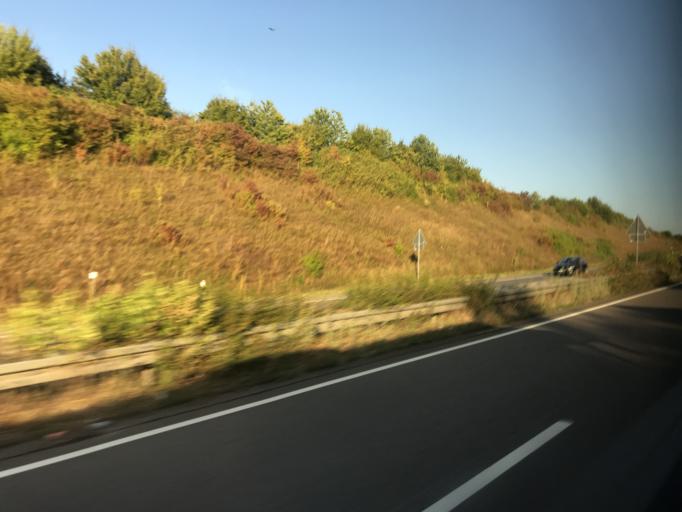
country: DE
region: Saarland
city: Perl
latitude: 49.4802
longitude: 6.4229
